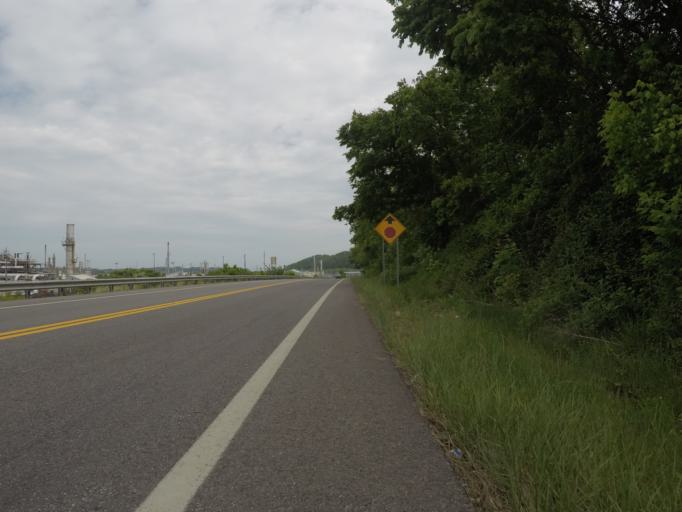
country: US
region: West Virginia
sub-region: Wayne County
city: Kenova
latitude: 38.3675
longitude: -82.5923
